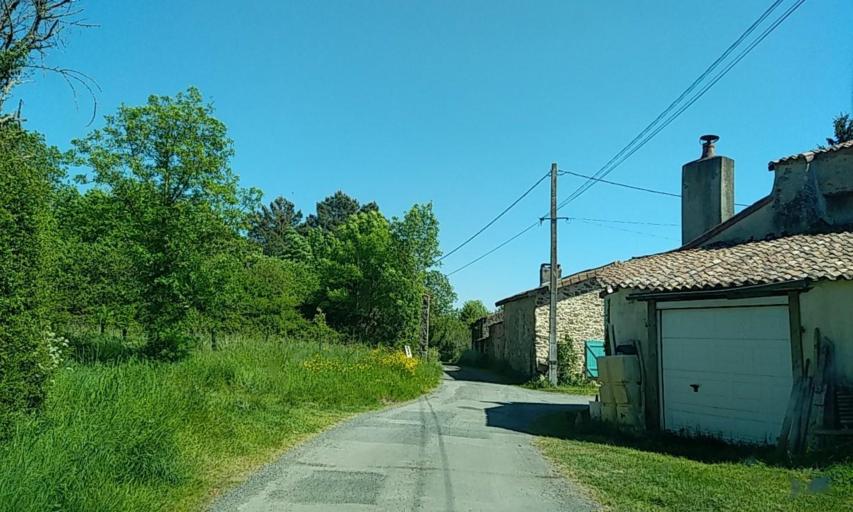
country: FR
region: Poitou-Charentes
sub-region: Departement des Deux-Sevres
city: Boisme
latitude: 46.7658
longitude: -0.4503
